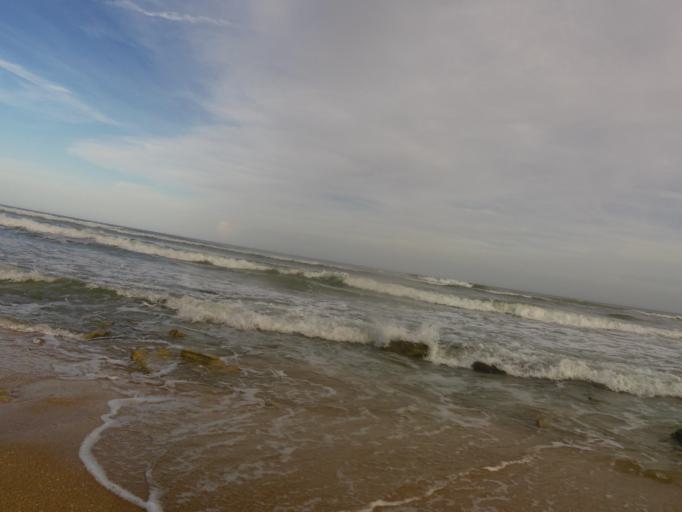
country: US
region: Florida
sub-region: Flagler County
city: Palm Coast
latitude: 29.6095
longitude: -81.1869
